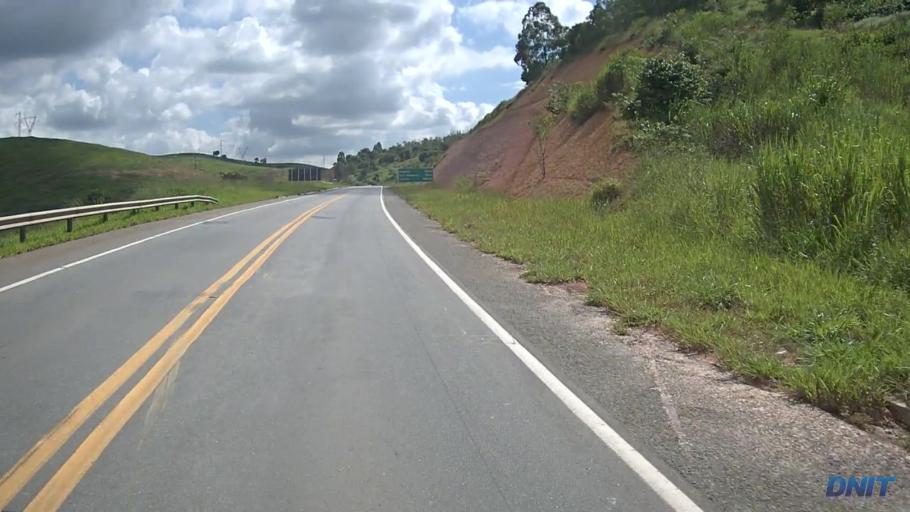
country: BR
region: Minas Gerais
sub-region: Belo Oriente
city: Belo Oriente
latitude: -19.1037
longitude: -42.2010
